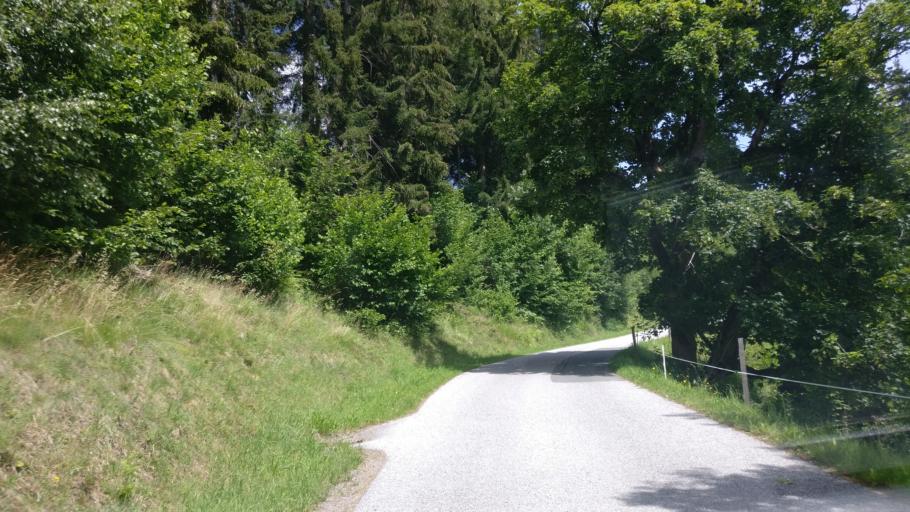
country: AT
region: Salzburg
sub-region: Politischer Bezirk Sankt Johann im Pongau
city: Filzmoos
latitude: 47.4021
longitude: 13.5255
